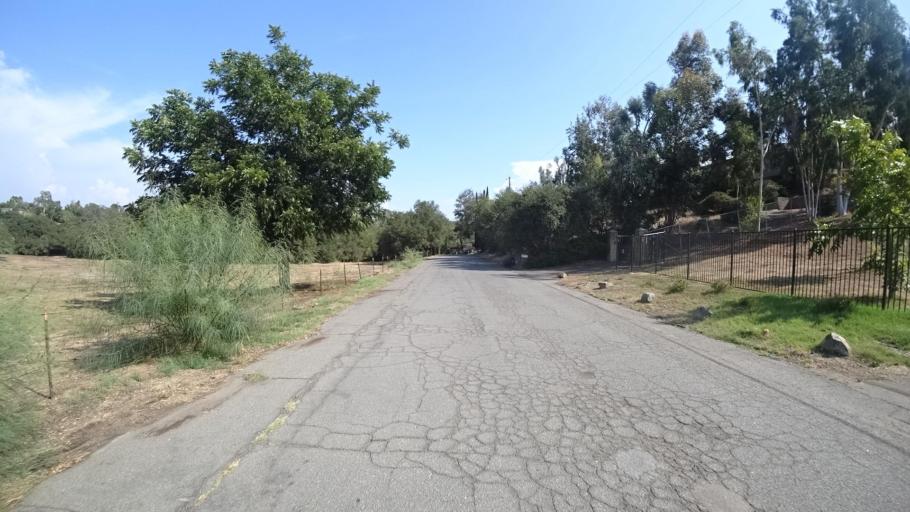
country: US
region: California
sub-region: San Diego County
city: Escondido
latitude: 33.1039
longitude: -117.0532
